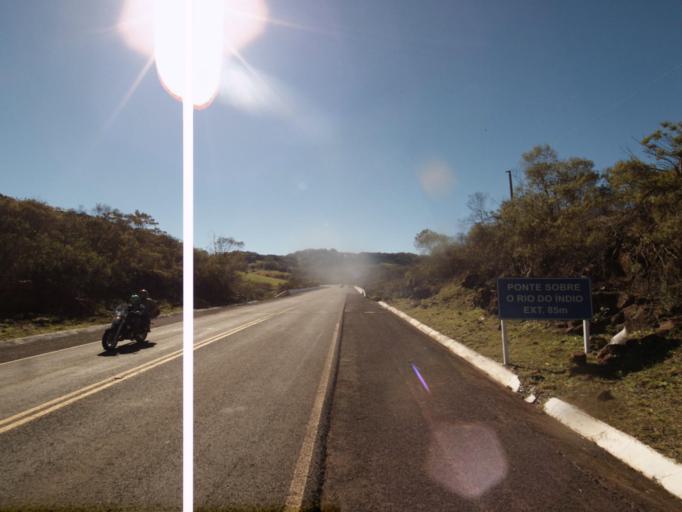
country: AR
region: Misiones
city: Bernardo de Irigoyen
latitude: -26.6560
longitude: -53.6078
